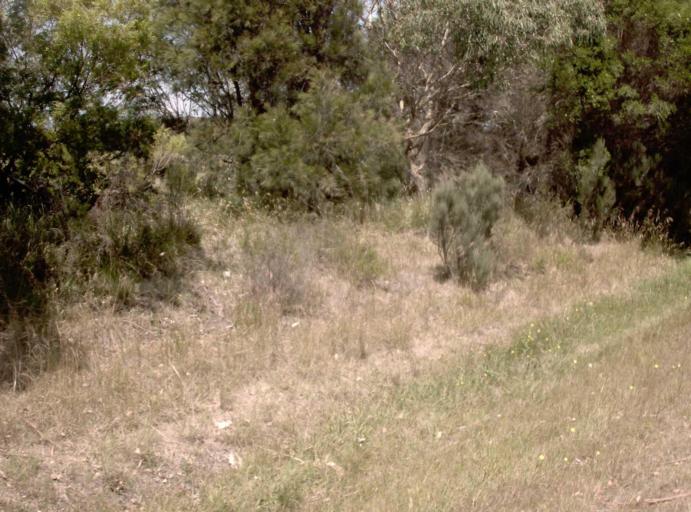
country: AU
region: Victoria
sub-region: Bass Coast
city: North Wonthaggi
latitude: -38.6182
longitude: 145.9615
